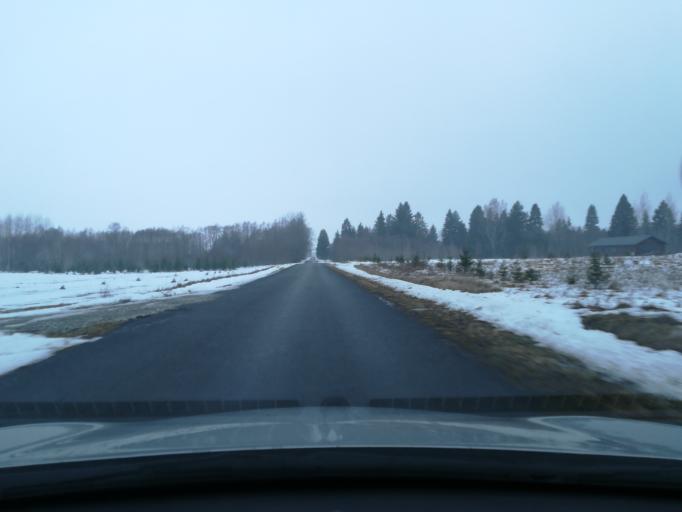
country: EE
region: Harju
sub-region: Raasiku vald
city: Raasiku
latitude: 59.3456
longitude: 25.2187
